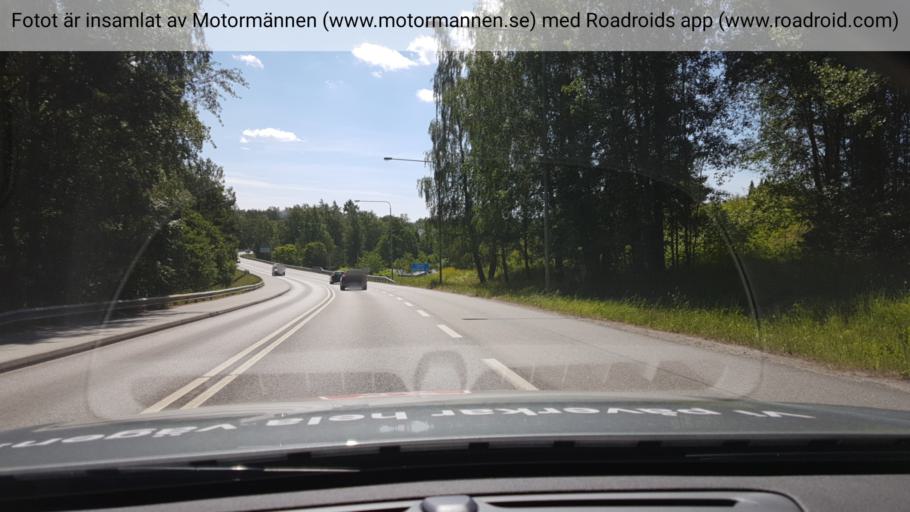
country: SE
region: Stockholm
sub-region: Tyreso Kommun
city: Bollmora
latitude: 59.2317
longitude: 18.1951
